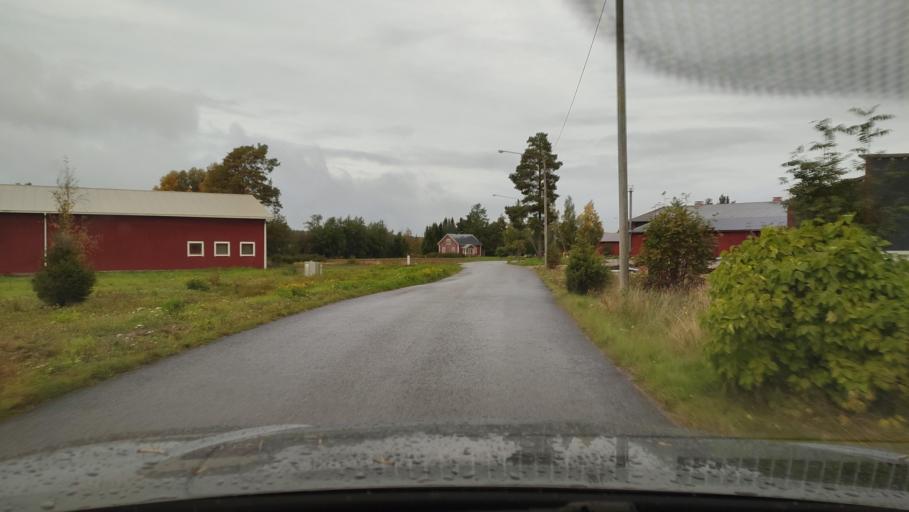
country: FI
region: Southern Ostrobothnia
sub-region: Suupohja
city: Karijoki
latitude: 62.2277
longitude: 21.6491
